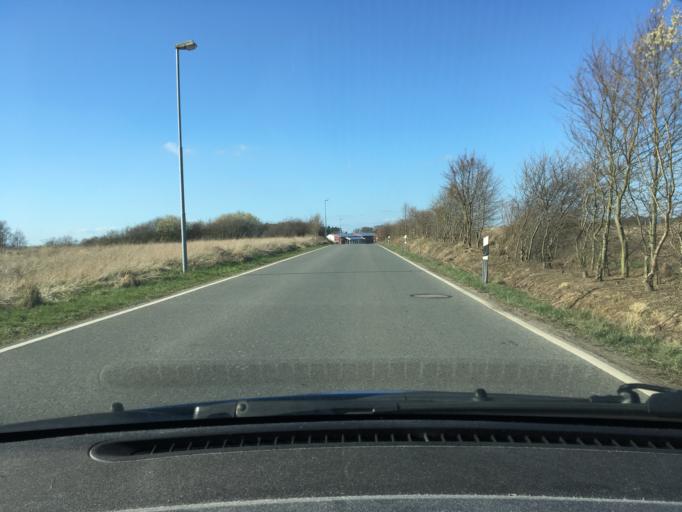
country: DE
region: Lower Saxony
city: Dahlem
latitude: 53.1910
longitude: 10.7497
